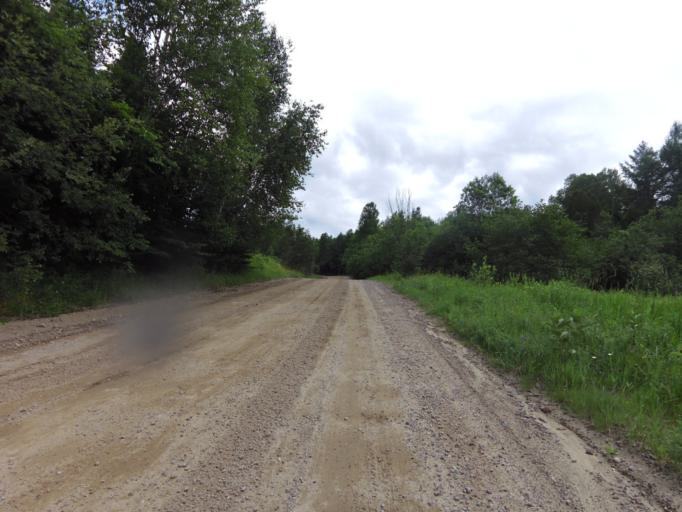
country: CA
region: Quebec
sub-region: Laurentides
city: Mont-Tremblant
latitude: 45.9415
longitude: -74.6491
